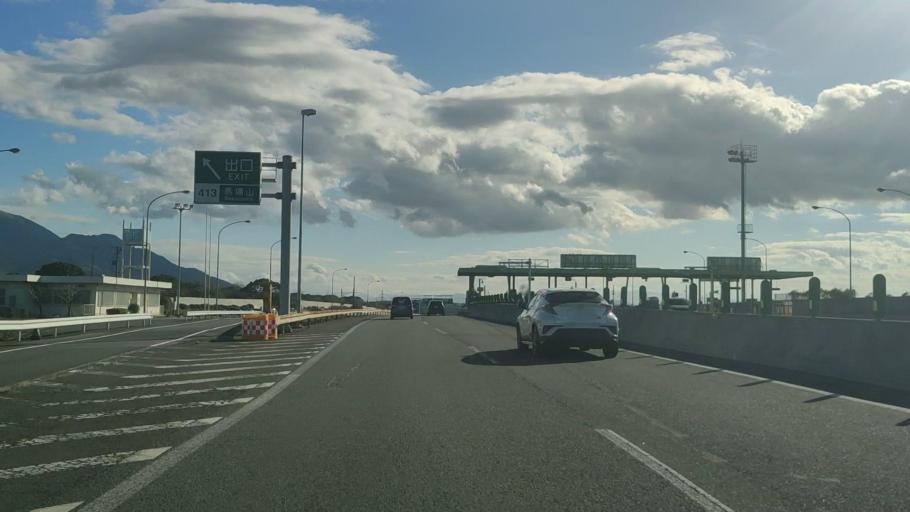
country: JP
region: Fukuoka
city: Nakama
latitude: 33.7967
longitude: 130.7437
